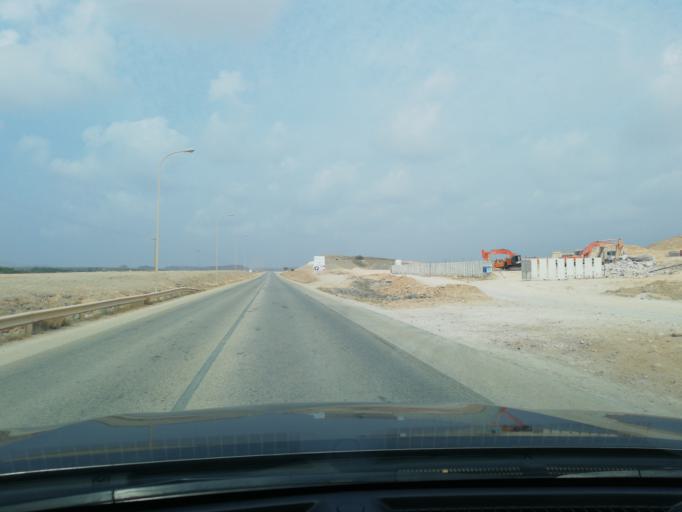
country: OM
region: Zufar
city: Salalah
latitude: 16.9465
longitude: 53.9557
